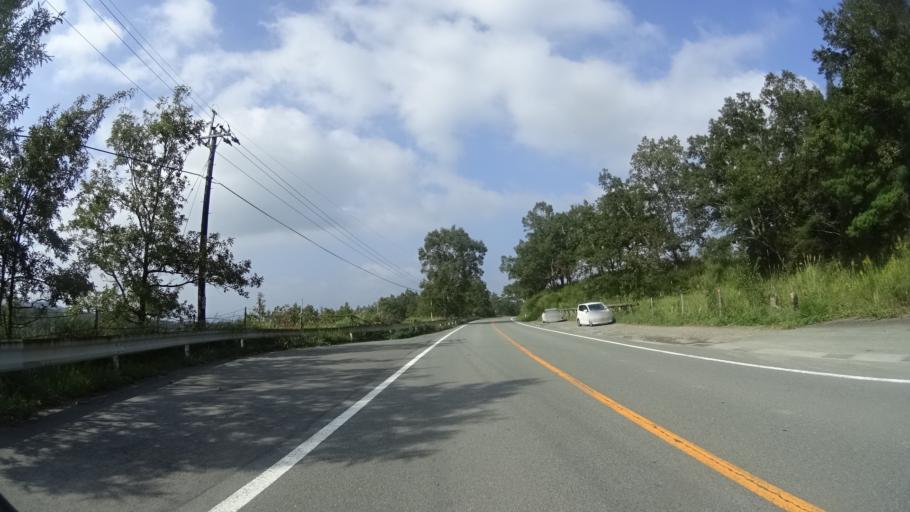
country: JP
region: Kumamoto
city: Aso
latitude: 33.0470
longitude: 131.0675
